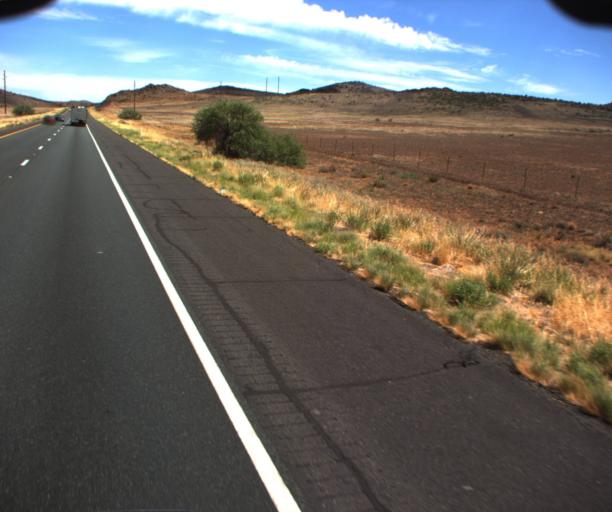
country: US
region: Arizona
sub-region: Yavapai County
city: Cordes Lakes
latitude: 34.4406
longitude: -112.0310
